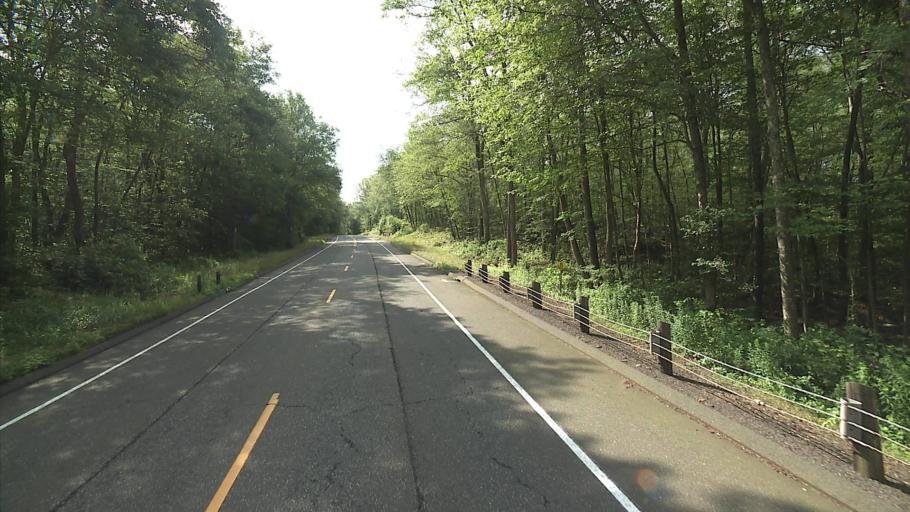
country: US
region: Connecticut
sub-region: Middlesex County
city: Chester Center
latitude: 41.3713
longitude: -72.5001
